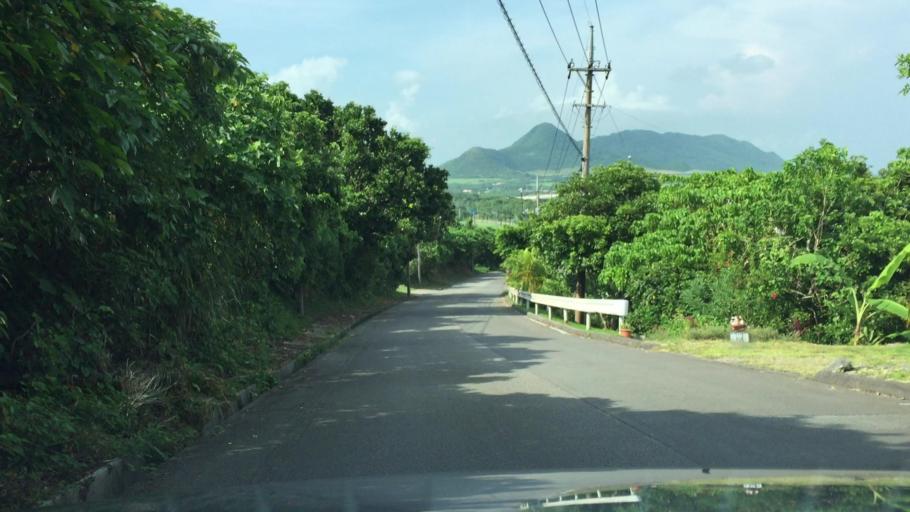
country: JP
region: Okinawa
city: Ishigaki
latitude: 24.4924
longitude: 124.2781
